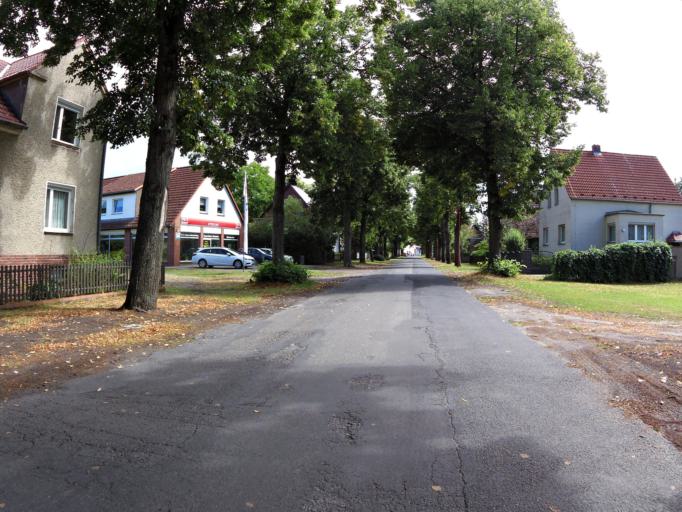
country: DE
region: Brandenburg
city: Storkow
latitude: 52.2523
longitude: 13.9223
